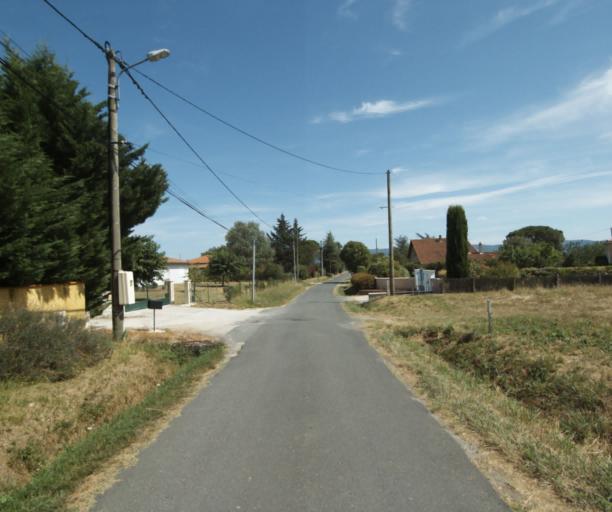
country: FR
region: Midi-Pyrenees
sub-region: Departement du Tarn
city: Puylaurens
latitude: 43.5338
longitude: 2.0163
